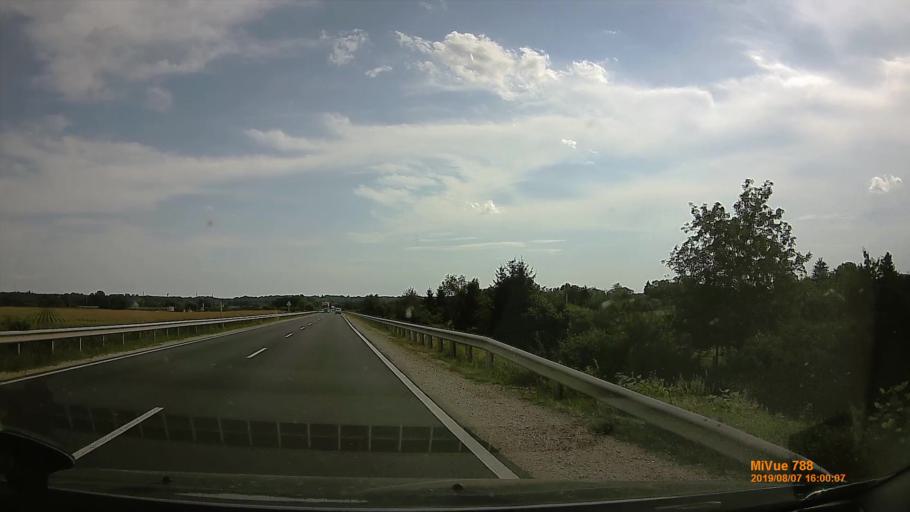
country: HU
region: Vas
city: Kormend
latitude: 47.0076
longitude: 16.6167
